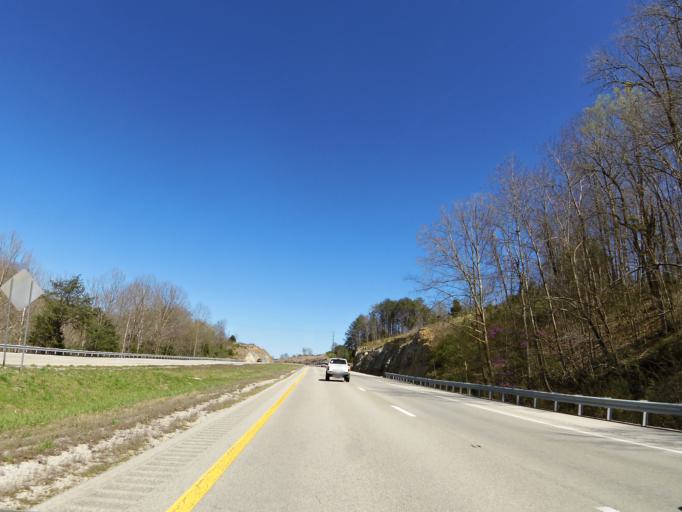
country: US
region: Kentucky
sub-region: Pulaski County
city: Somerset
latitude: 37.0990
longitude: -84.6795
